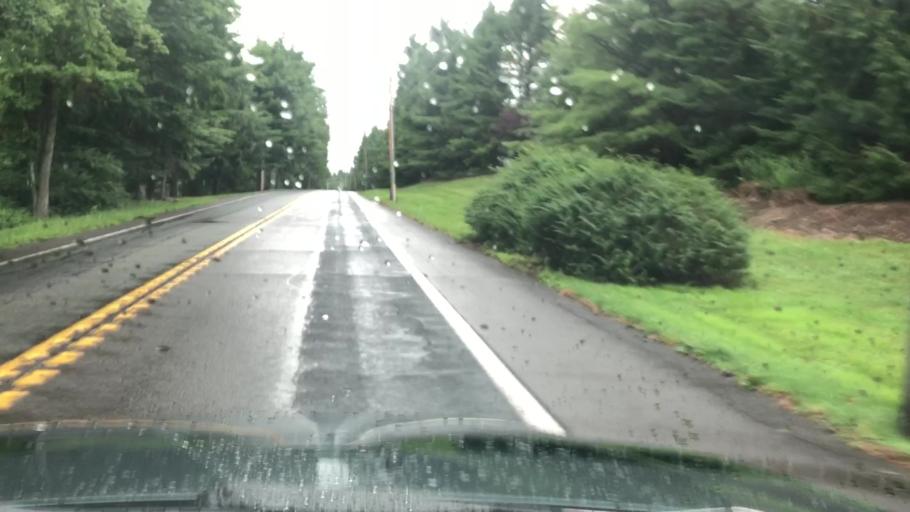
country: US
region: Pennsylvania
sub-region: Monroe County
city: Mountainhome
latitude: 41.2148
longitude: -75.2367
